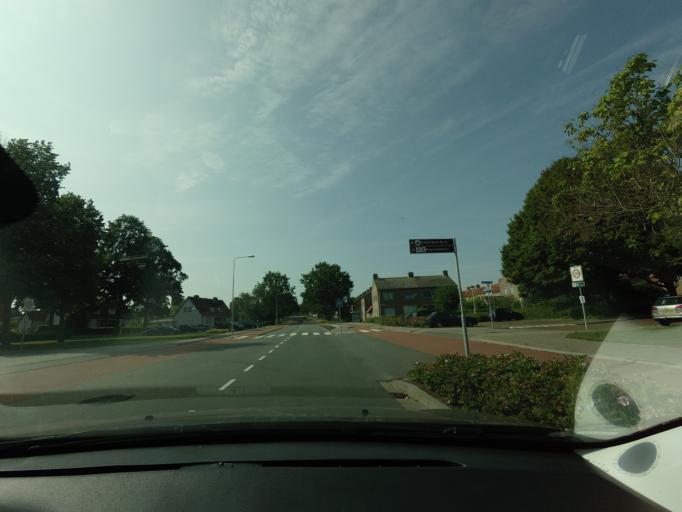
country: NL
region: South Holland
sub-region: Gemeente Papendrecht
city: Papendrecht
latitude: 51.8279
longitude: 4.6931
